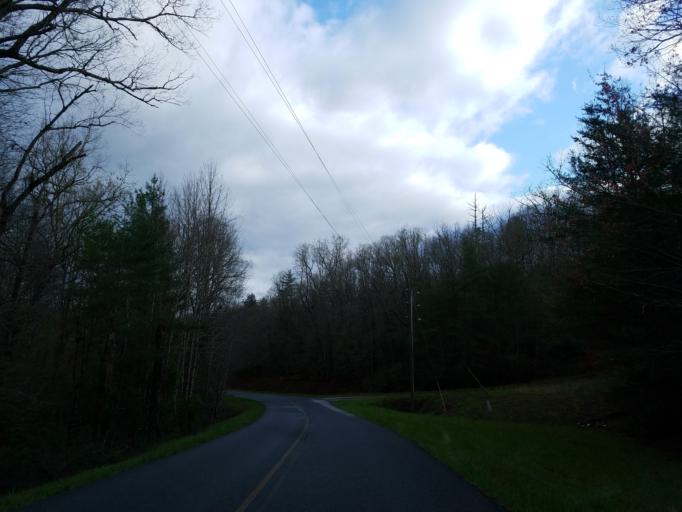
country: US
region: Georgia
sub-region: Fannin County
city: Blue Ridge
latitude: 34.7678
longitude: -84.2312
